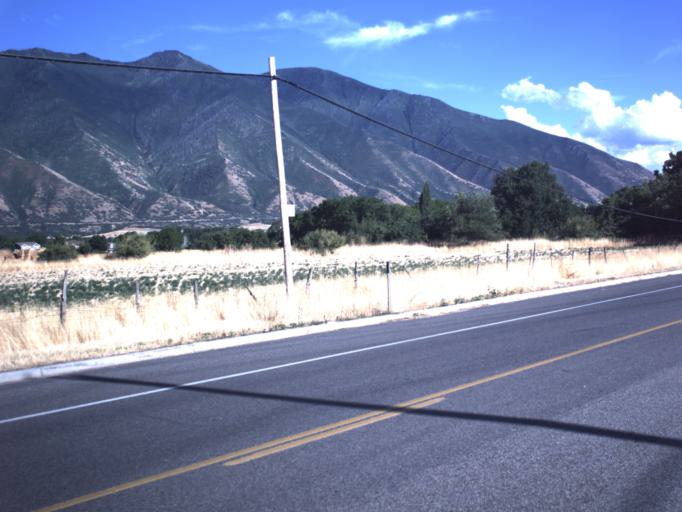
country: US
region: Utah
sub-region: Utah County
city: Mapleton
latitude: 40.1359
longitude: -111.5980
